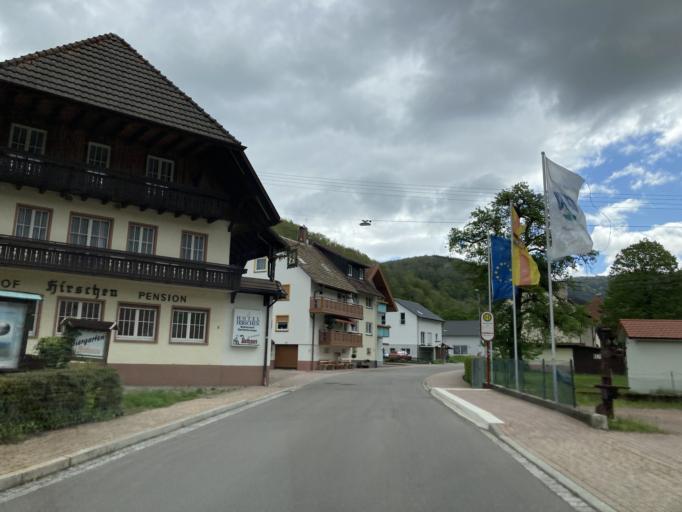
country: DE
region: Baden-Wuerttemberg
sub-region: Freiburg Region
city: Muhlenbach
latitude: 48.2133
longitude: 8.1432
